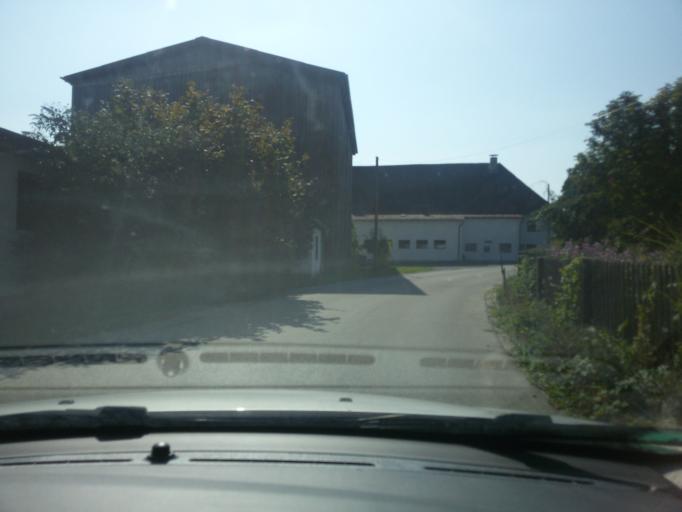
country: DE
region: Bavaria
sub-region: Swabia
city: Hiltenfingen
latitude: 48.1828
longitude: 10.6833
